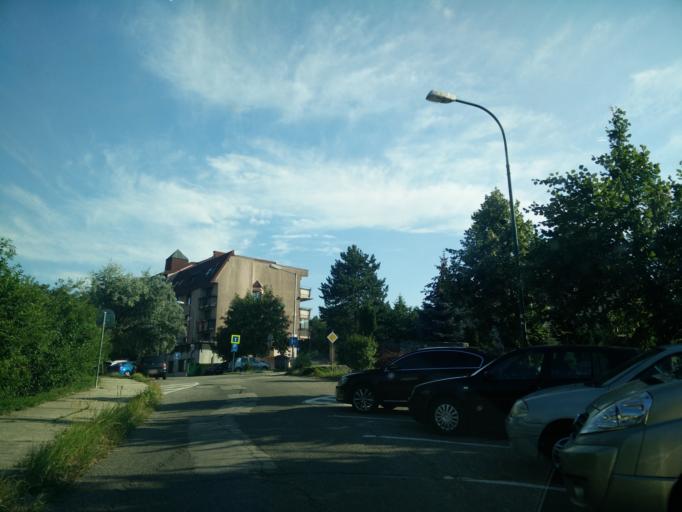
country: AT
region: Lower Austria
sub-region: Politischer Bezirk Bruck an der Leitha
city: Wolfsthal
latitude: 48.1948
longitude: 17.0241
